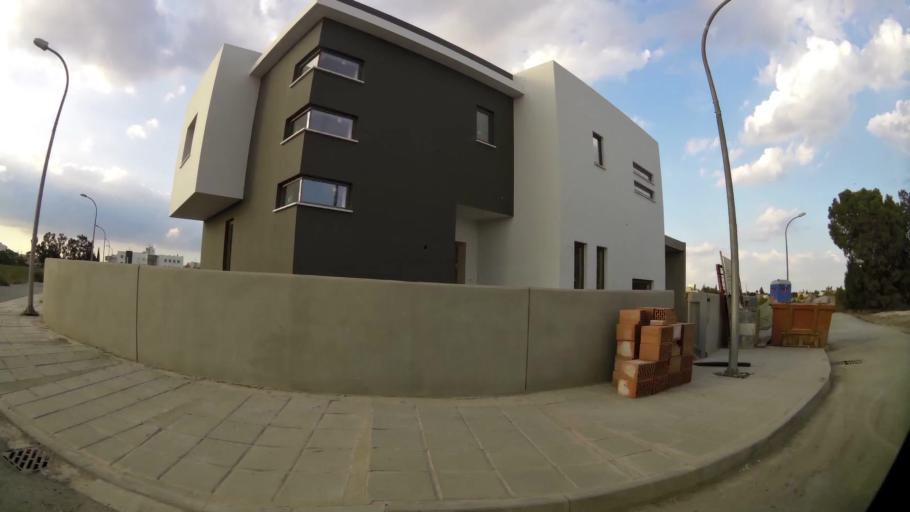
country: CY
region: Larnaka
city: Kiti
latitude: 34.8527
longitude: 33.5847
